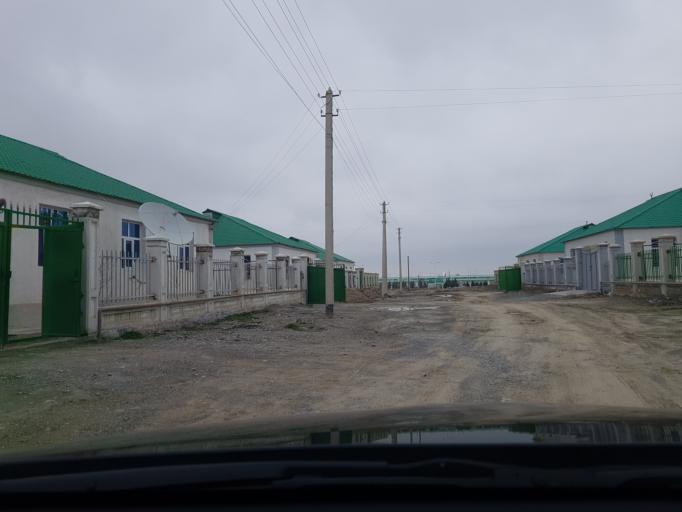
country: TM
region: Ahal
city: Arcabil
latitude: 38.1313
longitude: 57.9424
